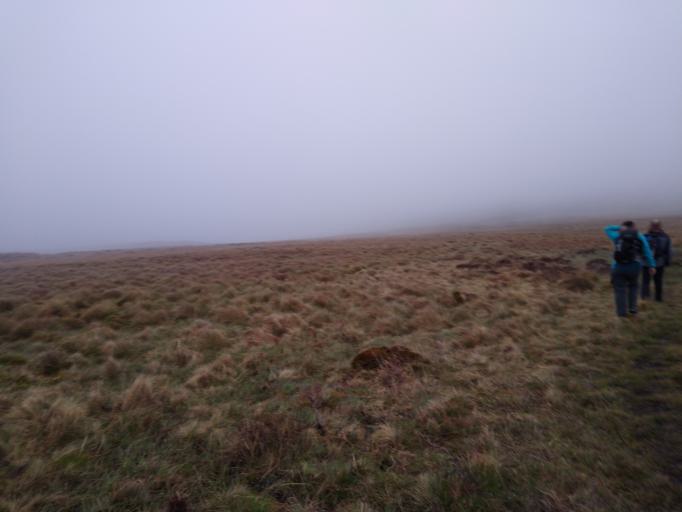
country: GB
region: England
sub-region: Cumbria
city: Keswick
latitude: 54.5372
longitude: -3.0961
